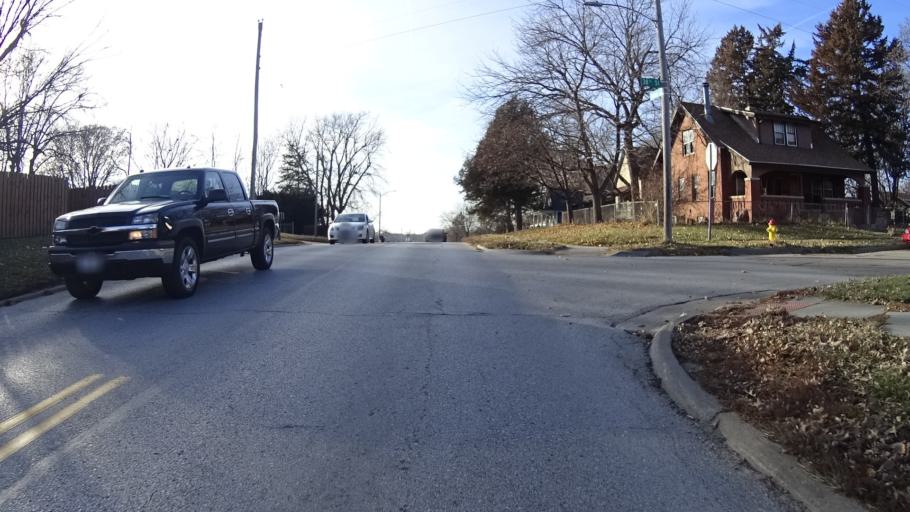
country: US
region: Nebraska
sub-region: Sarpy County
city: La Vista
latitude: 41.1909
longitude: -95.9699
